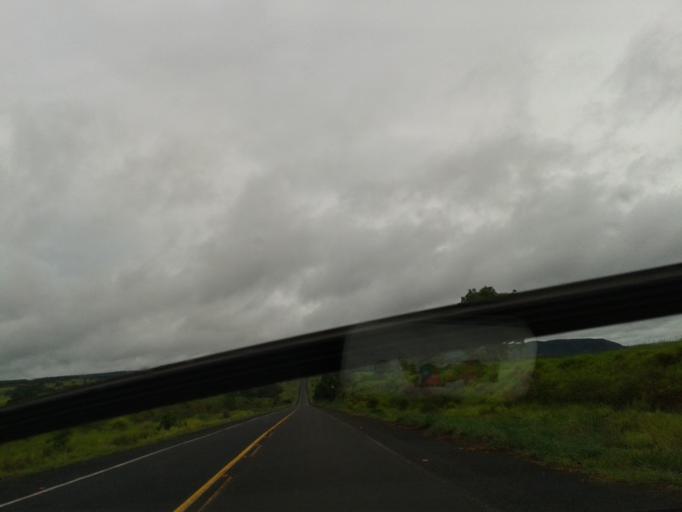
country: BR
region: Minas Gerais
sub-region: Santa Vitoria
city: Santa Vitoria
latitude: -19.2448
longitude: -50.0136
